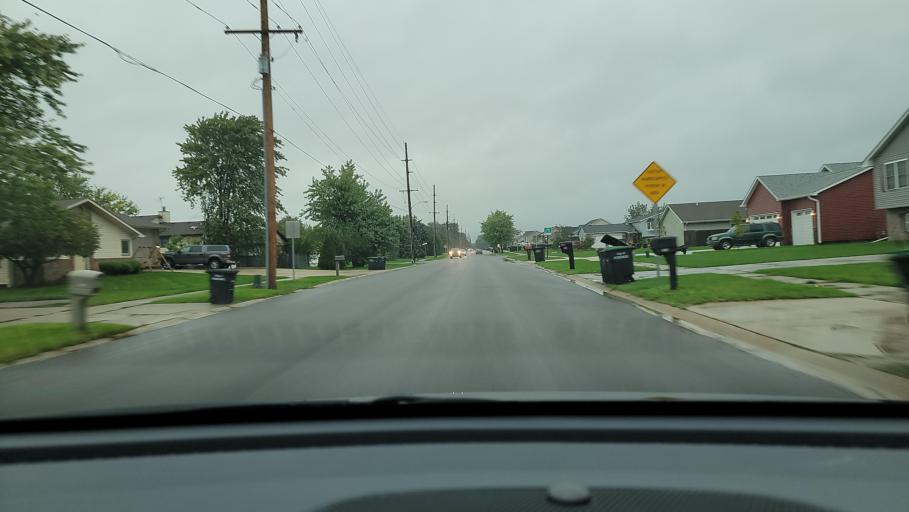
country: US
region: Indiana
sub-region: Porter County
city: Portage
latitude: 41.5618
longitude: -87.1634
